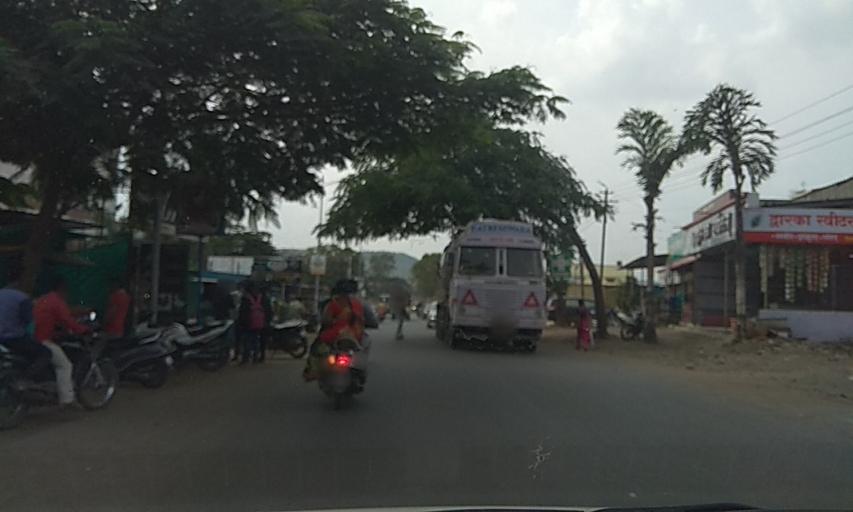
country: IN
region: Maharashtra
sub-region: Pune Division
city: Pimpri
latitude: 18.5762
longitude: 73.7110
